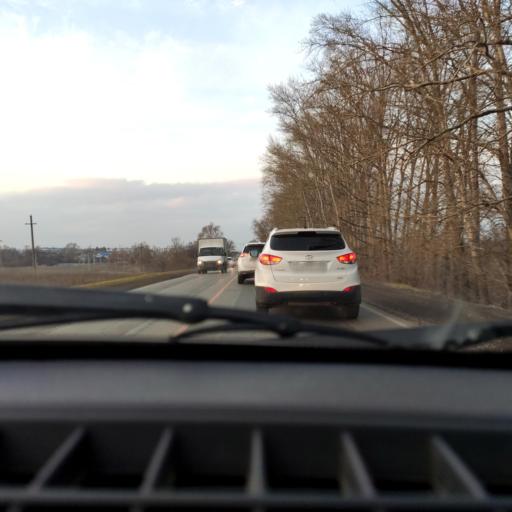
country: RU
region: Bashkortostan
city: Avdon
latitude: 54.7308
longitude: 55.8049
